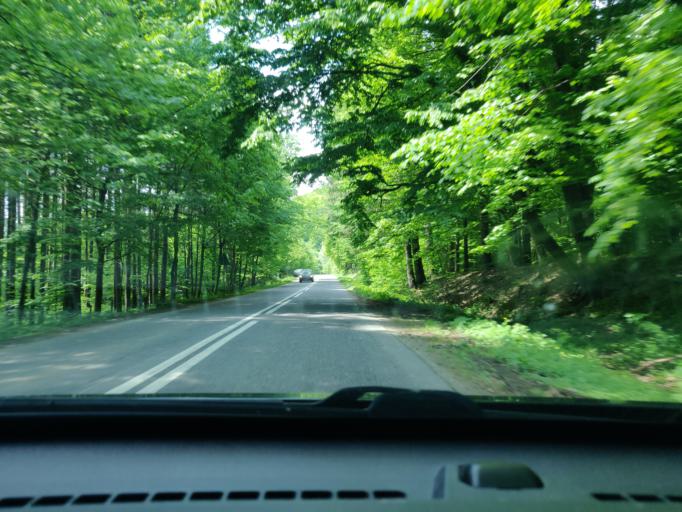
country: RO
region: Vrancea
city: Dragosloveni
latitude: 46.0312
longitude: 26.6930
